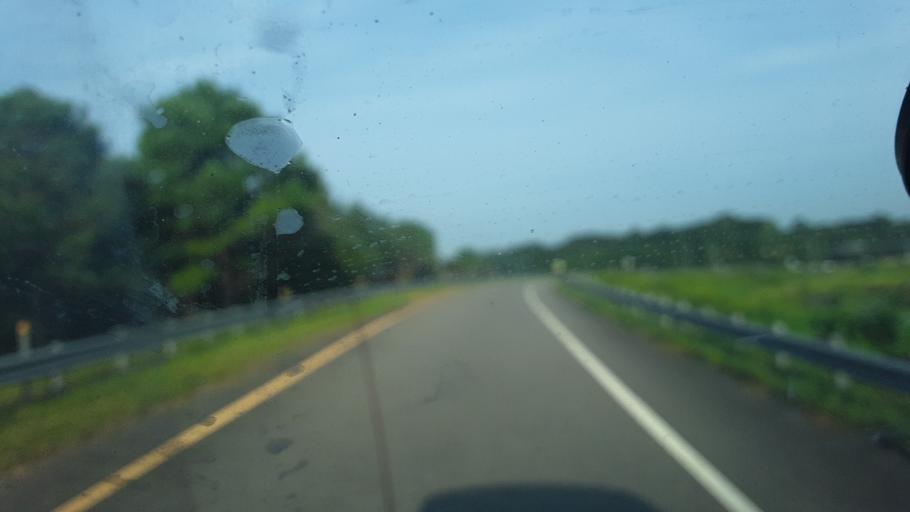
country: US
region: South Carolina
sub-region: Horry County
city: Myrtle Beach
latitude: 33.7554
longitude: -78.8520
